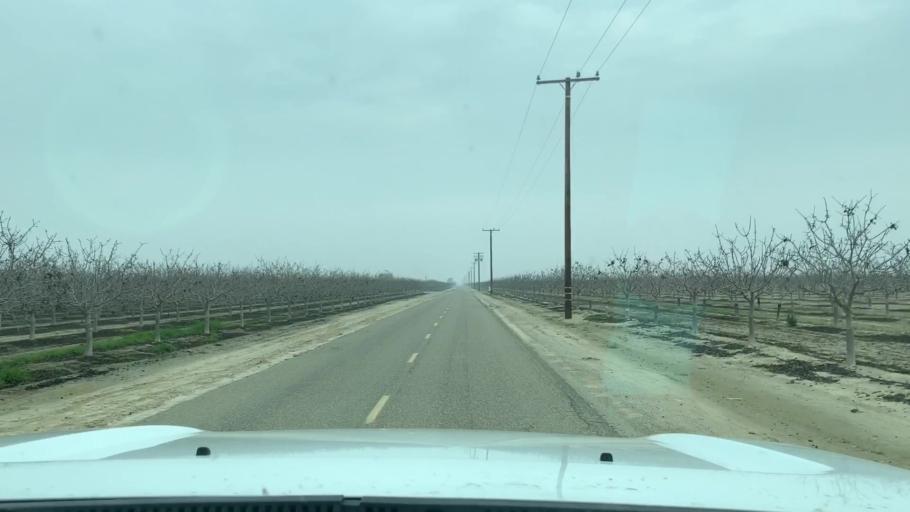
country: US
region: California
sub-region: Tulare County
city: Earlimart
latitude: 35.8193
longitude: -119.3466
